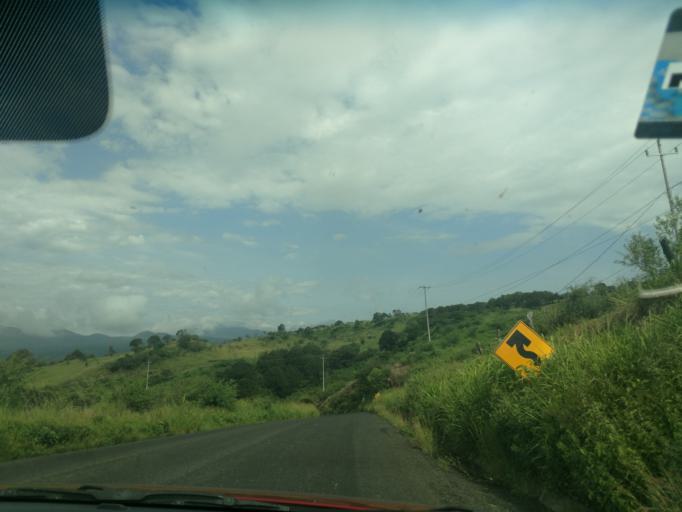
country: MX
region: Jalisco
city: El Salto
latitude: 20.4320
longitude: -104.4767
